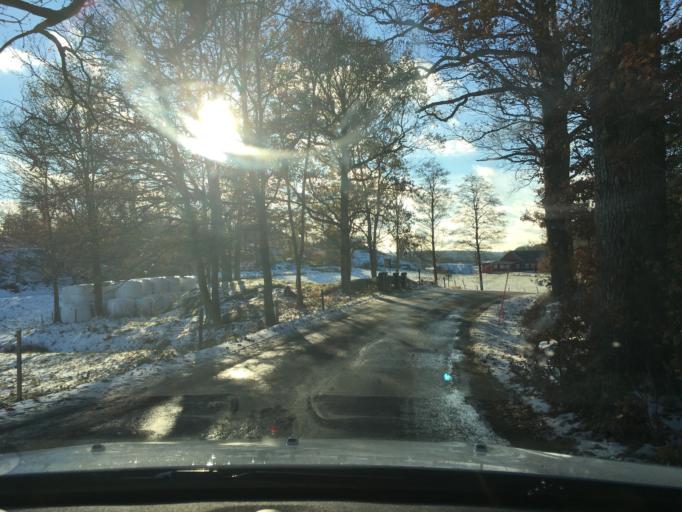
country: SE
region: Vaestra Goetaland
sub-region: Tjorns Kommun
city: Myggenas
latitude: 58.0901
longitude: 11.7535
